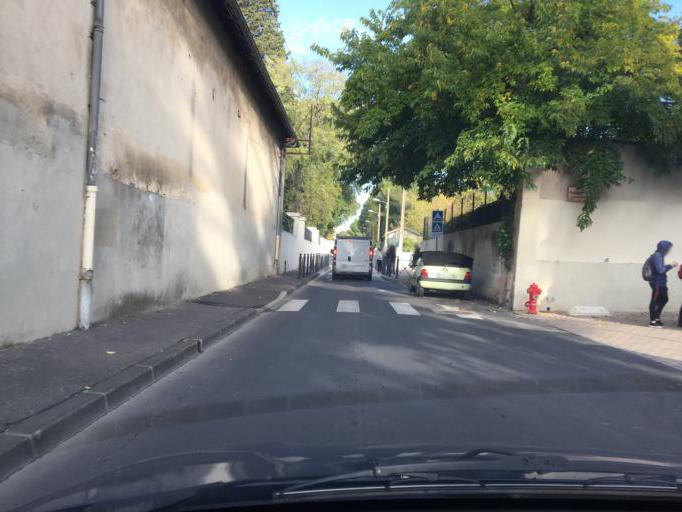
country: FR
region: Languedoc-Roussillon
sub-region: Departement de l'Herault
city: Montpellier
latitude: 43.6189
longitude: 3.8778
